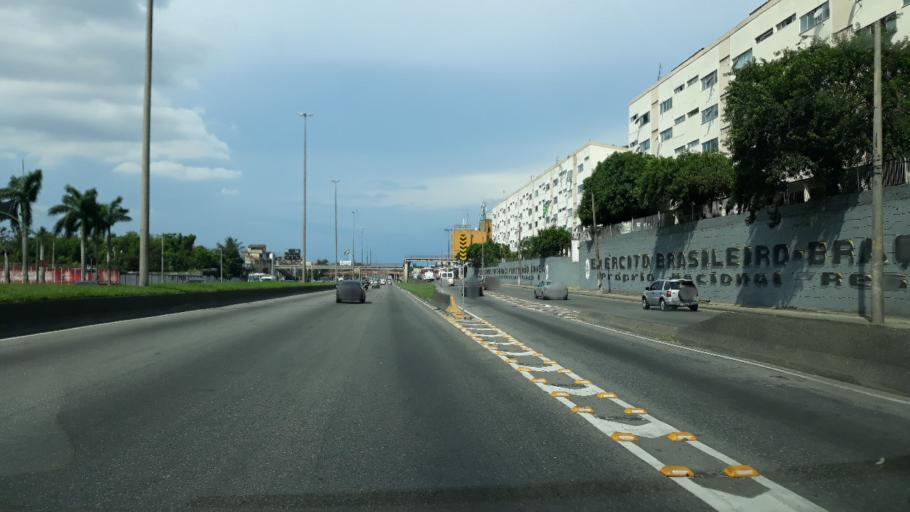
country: BR
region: Rio de Janeiro
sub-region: Sao Joao De Meriti
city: Sao Joao de Meriti
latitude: -22.8478
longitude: -43.3816
